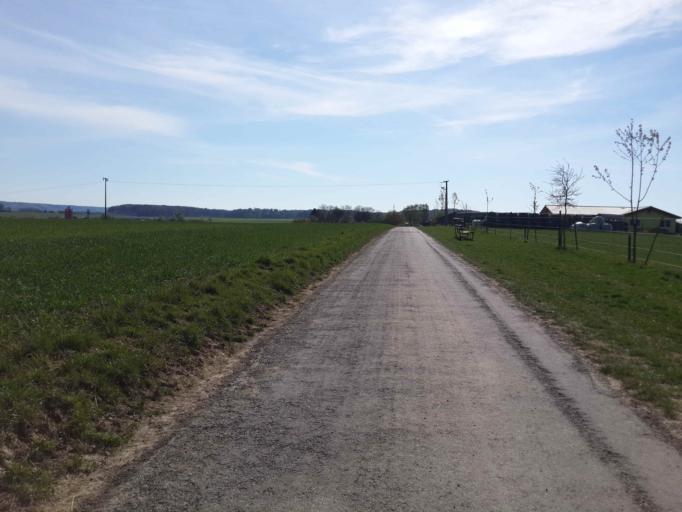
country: DE
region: Baden-Wuerttemberg
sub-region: Regierungsbezirk Stuttgart
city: Massenbachhausen
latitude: 49.1764
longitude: 9.0612
